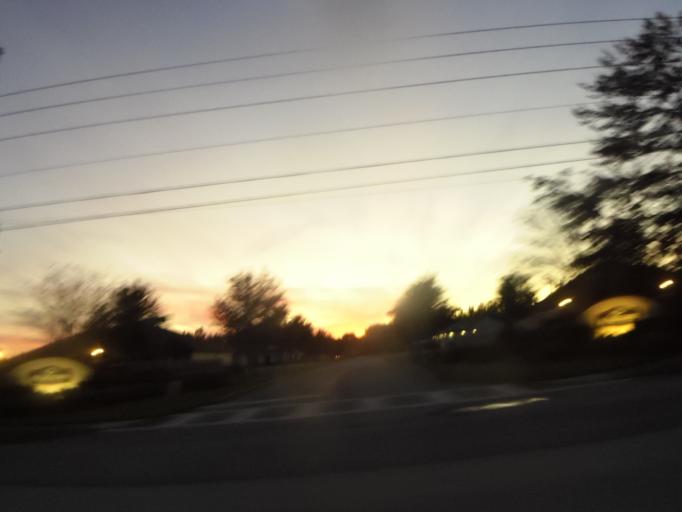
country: US
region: Florida
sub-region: Saint Johns County
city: Saint Augustine South
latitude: 29.8254
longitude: -81.3495
